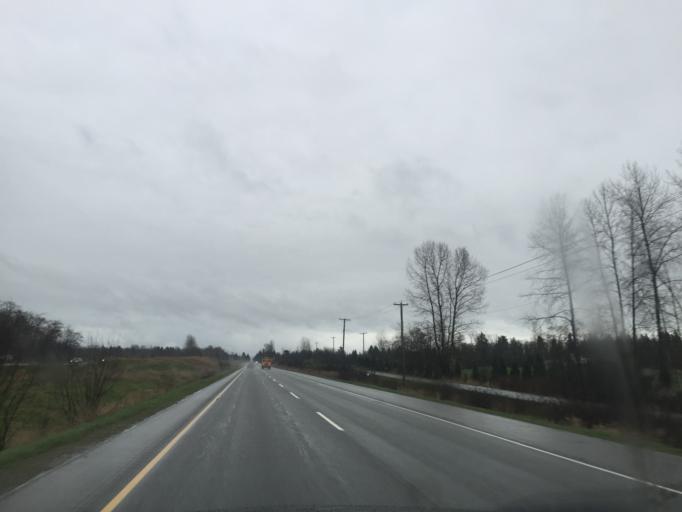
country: CA
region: British Columbia
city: Aldergrove
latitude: 49.0875
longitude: -122.4575
